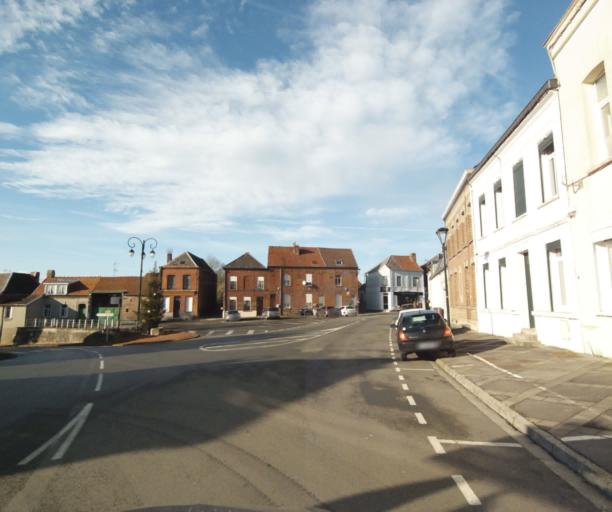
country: FR
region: Nord-Pas-de-Calais
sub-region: Departement du Nord
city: Preseau
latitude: 50.3100
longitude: 3.5732
